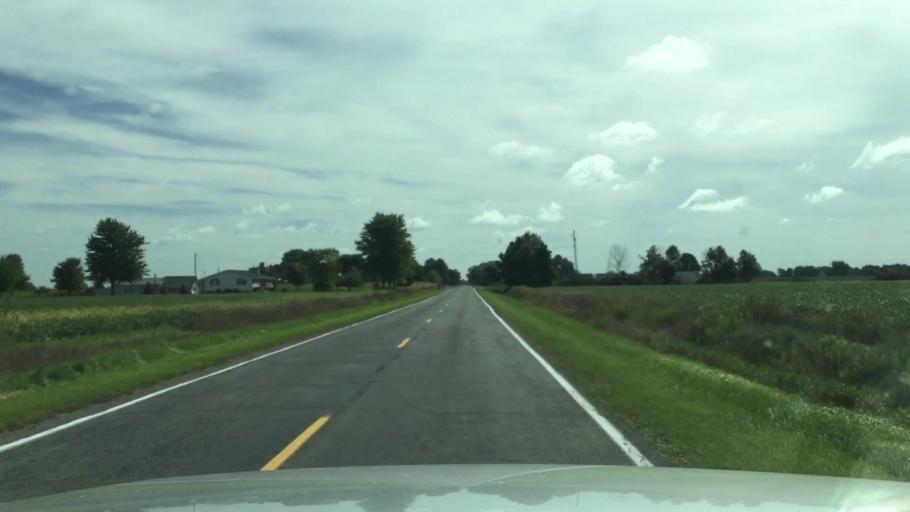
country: US
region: Michigan
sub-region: Saginaw County
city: Chesaning
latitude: 43.1465
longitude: -84.0055
